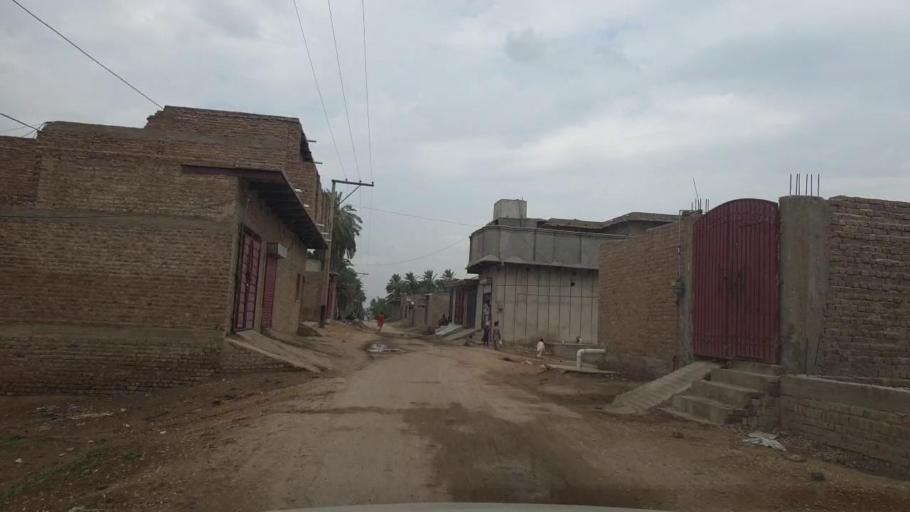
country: PK
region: Sindh
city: Khairpur
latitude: 27.5408
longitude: 68.7484
